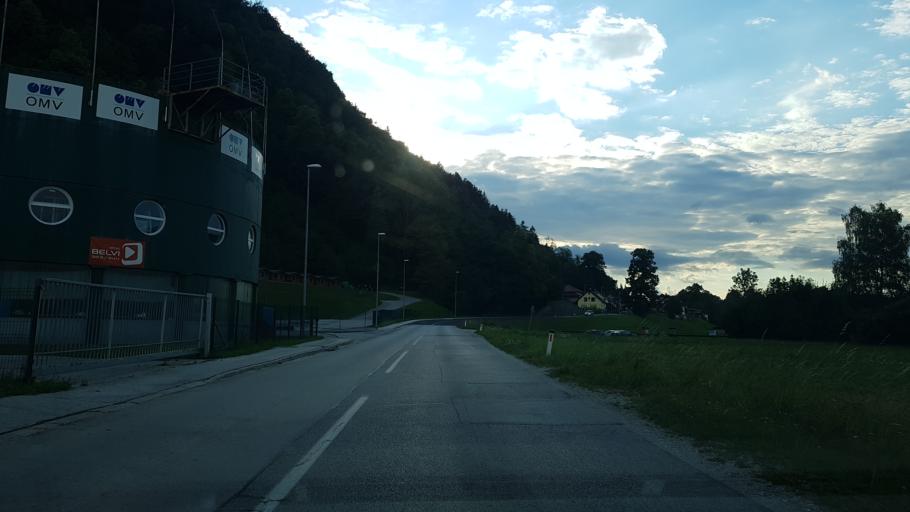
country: SI
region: Kranj
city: Kranj
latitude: 46.2451
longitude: 14.3436
